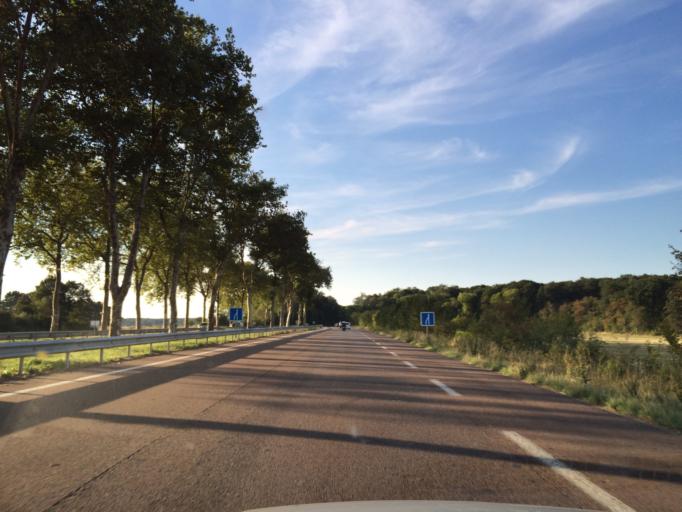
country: FR
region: Bourgogne
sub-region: Departement de l'Yonne
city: Auxerre
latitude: 47.8263
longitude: 3.5556
